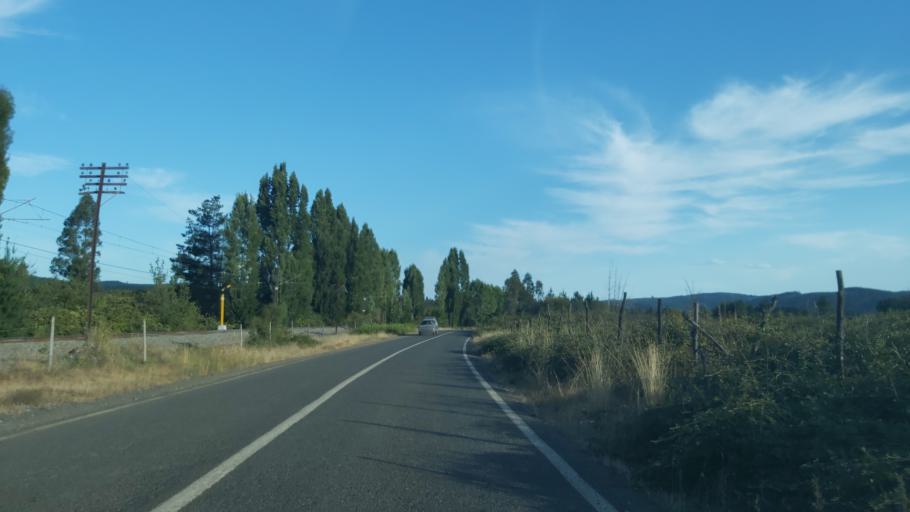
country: CL
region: Biobio
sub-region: Provincia de Concepcion
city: Lota
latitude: -37.1502
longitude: -72.9199
